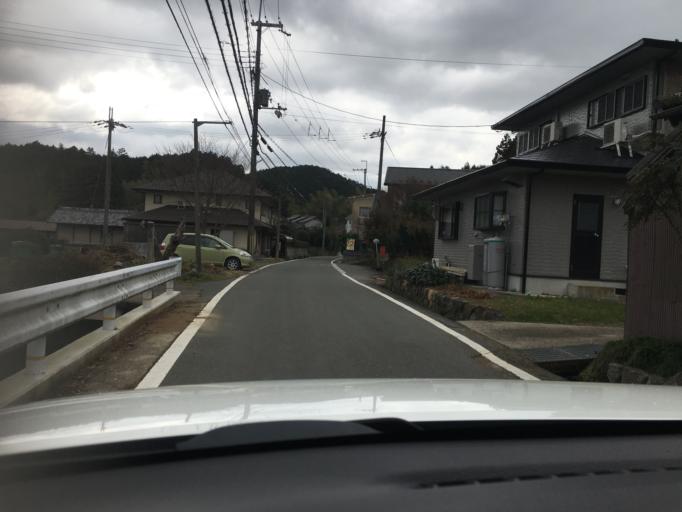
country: JP
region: Kyoto
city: Kameoka
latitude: 35.0433
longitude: 135.4748
